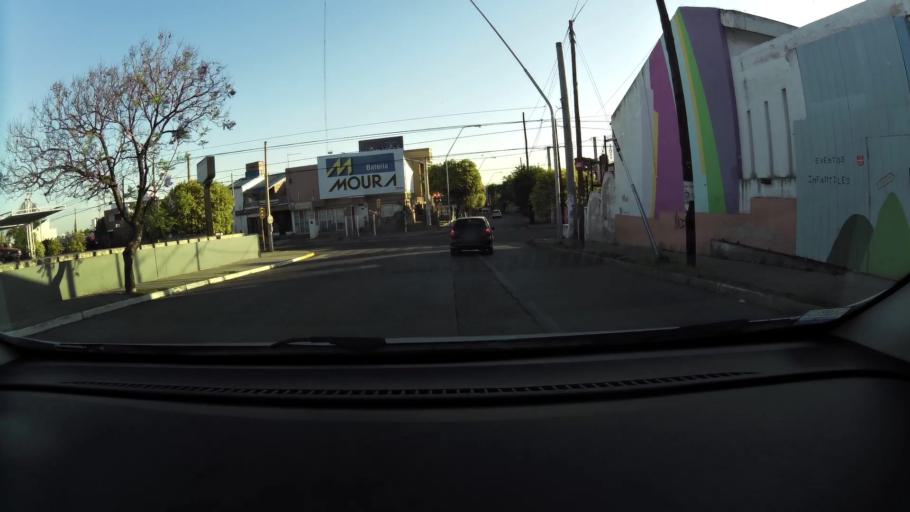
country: AR
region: Cordoba
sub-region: Departamento de Capital
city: Cordoba
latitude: -31.3822
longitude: -64.2160
